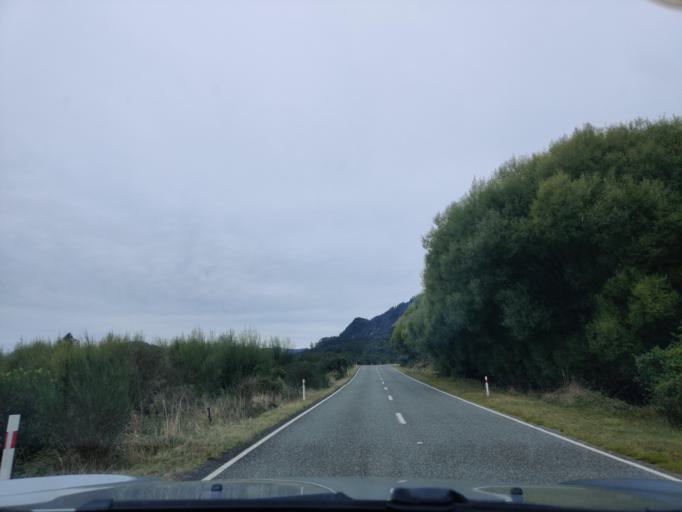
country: NZ
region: West Coast
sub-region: Buller District
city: Westport
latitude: -41.8575
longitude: 171.8716
